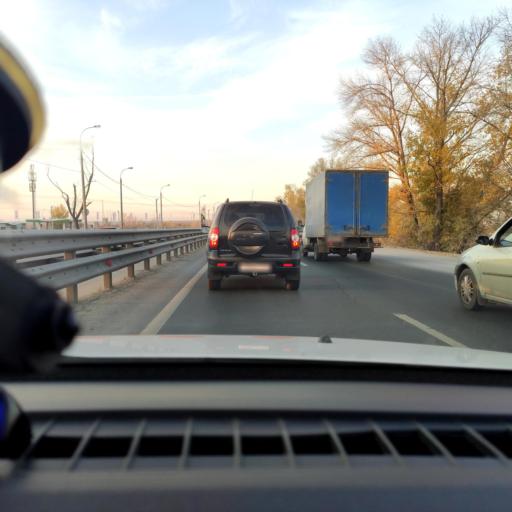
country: RU
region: Samara
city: Samara
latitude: 53.0977
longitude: 50.1582
